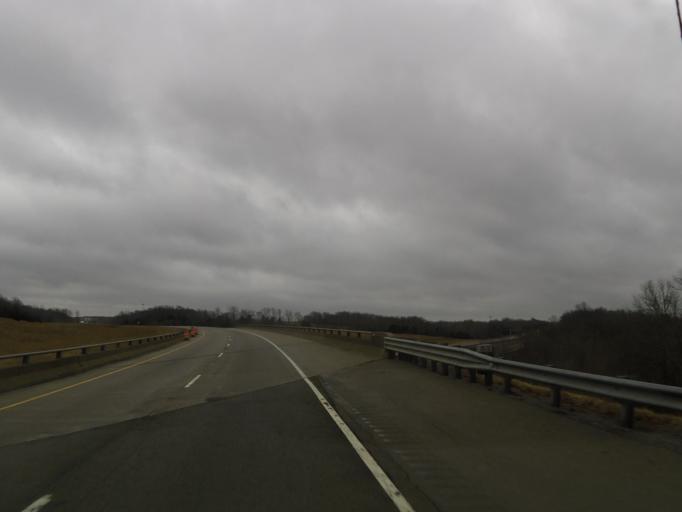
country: US
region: Illinois
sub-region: Johnson County
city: Goreville
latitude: 37.6037
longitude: -88.9977
